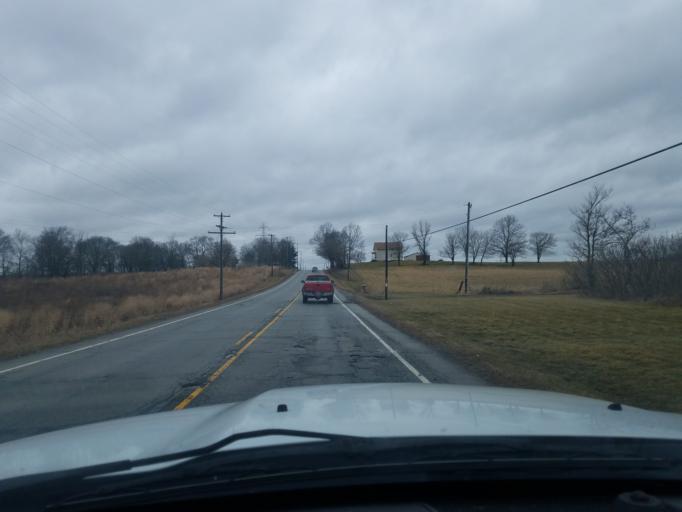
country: US
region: Indiana
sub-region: Noble County
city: Rome City
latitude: 41.4529
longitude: -85.3797
